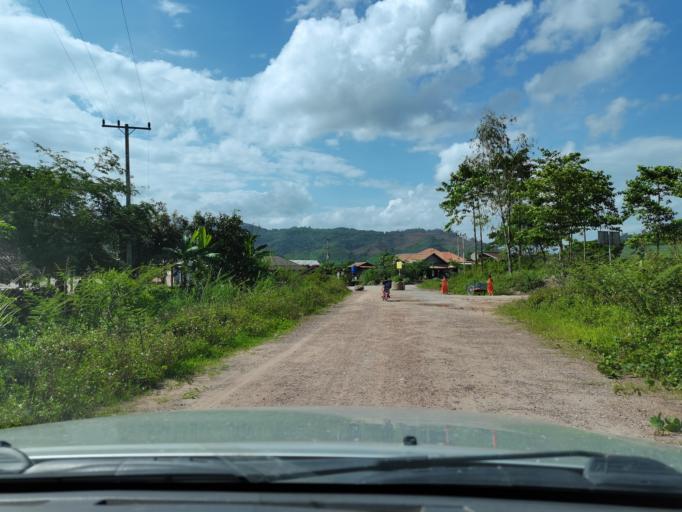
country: LA
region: Loungnamtha
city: Muang Nale
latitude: 20.5909
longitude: 101.0585
